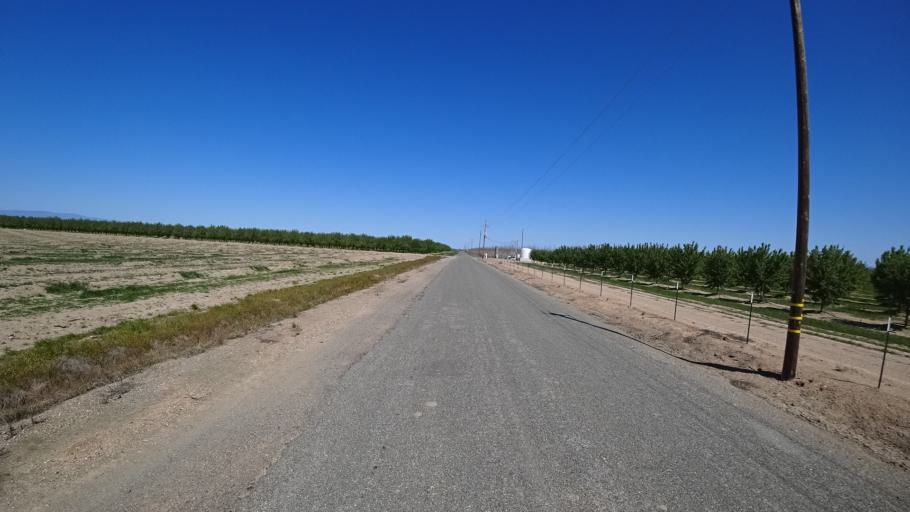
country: US
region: California
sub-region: Glenn County
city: Orland
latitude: 39.6817
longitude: -122.2343
